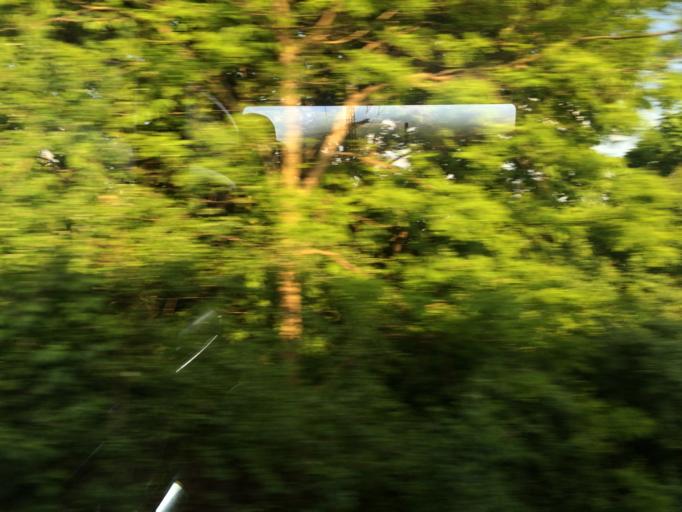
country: DE
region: North Rhine-Westphalia
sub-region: Regierungsbezirk Dusseldorf
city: Duisburg
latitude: 51.4155
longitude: 6.7739
